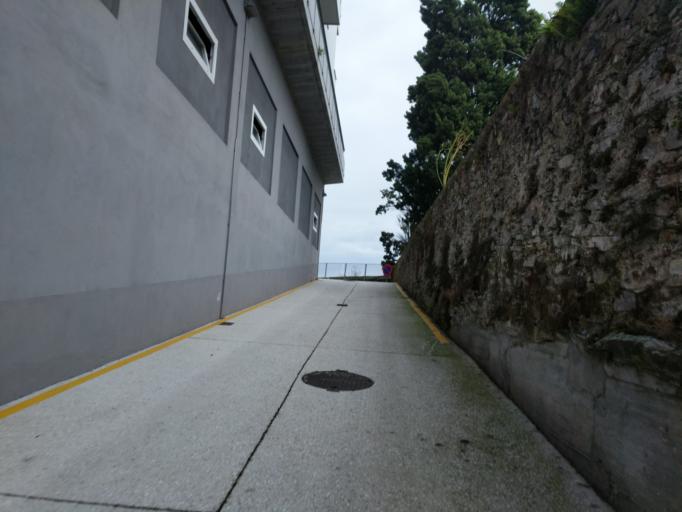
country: ES
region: Asturias
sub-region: Province of Asturias
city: Tineo
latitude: 43.3325
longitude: -6.4173
